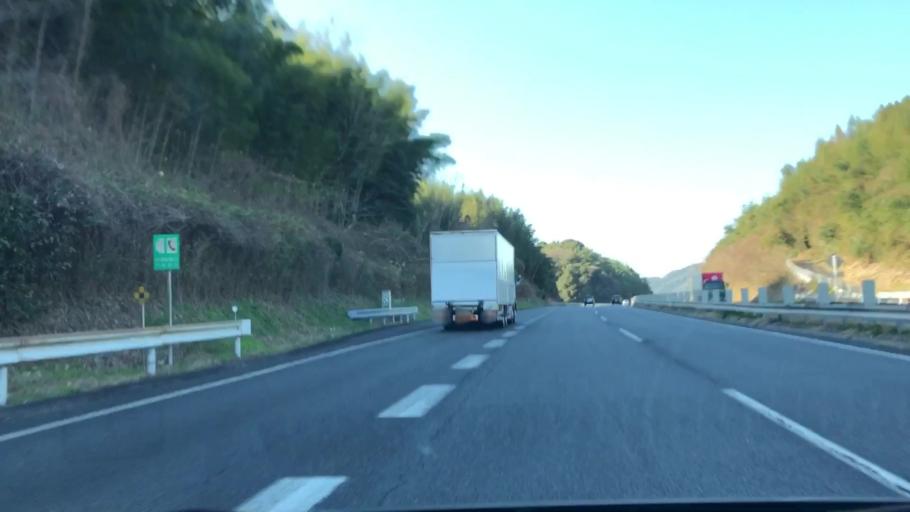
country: JP
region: Yamaguchi
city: Kudamatsu
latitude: 34.0323
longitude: 131.9334
